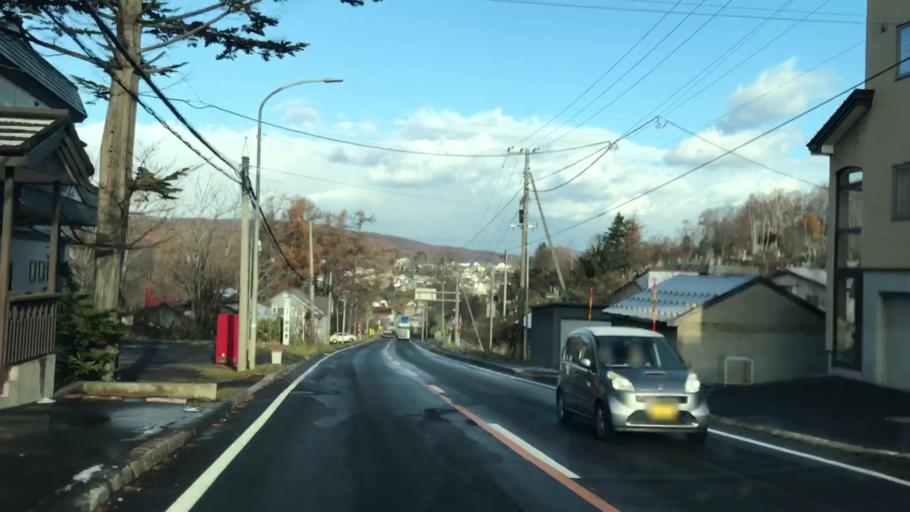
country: JP
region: Hokkaido
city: Otaru
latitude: 43.1637
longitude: 140.9974
